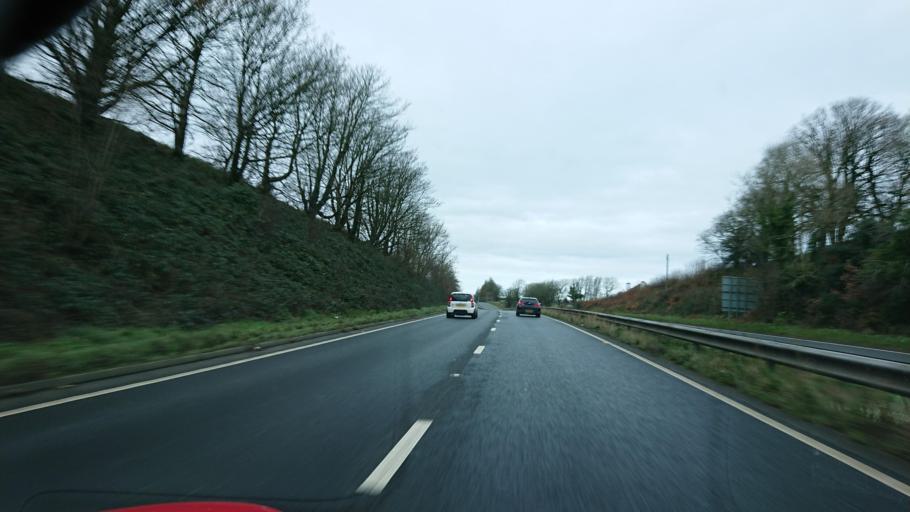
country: GB
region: England
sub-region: Cornwall
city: Liskeard
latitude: 50.4388
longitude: -4.4418
